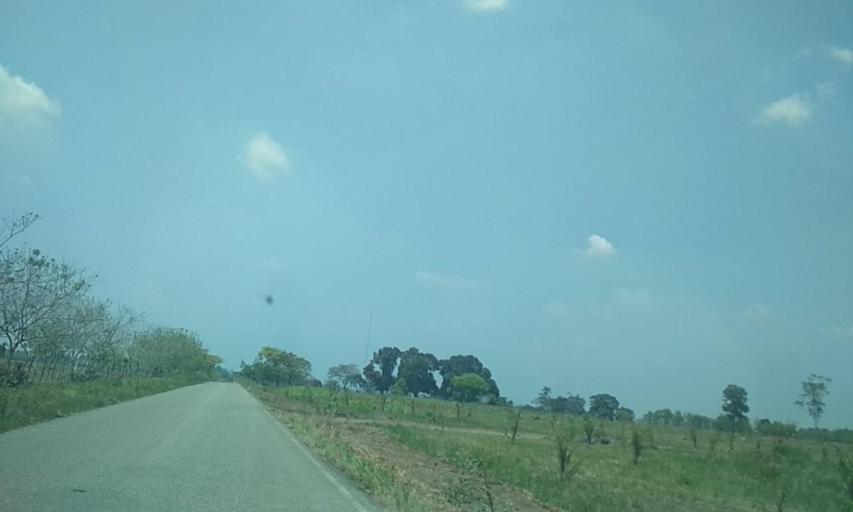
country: MX
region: Tabasco
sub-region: Huimanguillo
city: Paso de la Mina 3ra. Seccion
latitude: 17.8347
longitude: -93.6162
